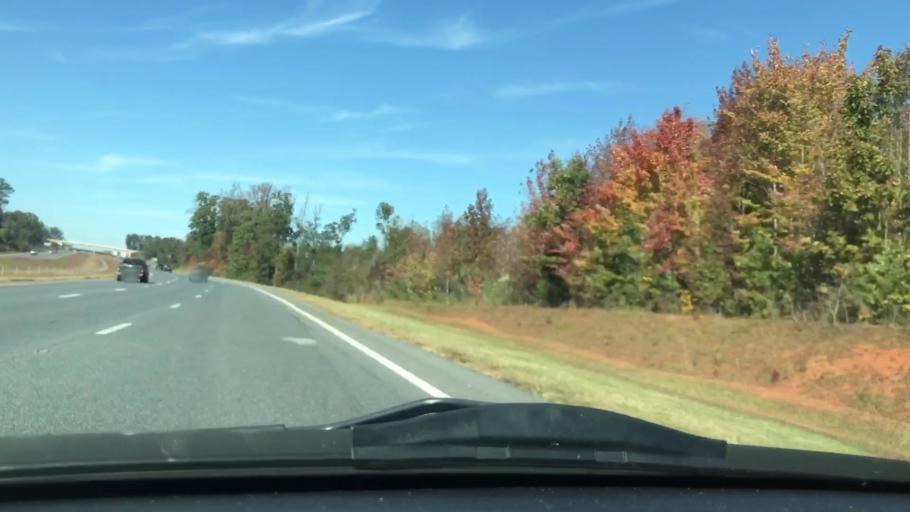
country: US
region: North Carolina
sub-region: Randolph County
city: Randleman
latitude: 35.8255
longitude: -79.8555
